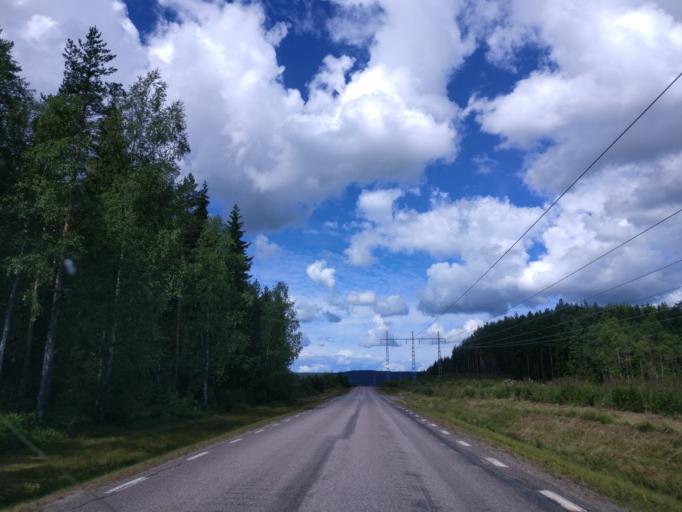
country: SE
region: Vaermland
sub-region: Hagfors Kommun
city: Hagfors
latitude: 60.0401
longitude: 13.5391
